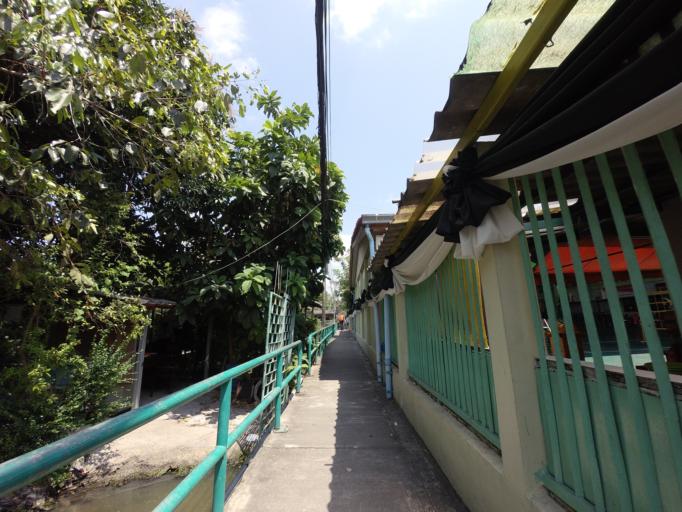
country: TH
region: Bangkok
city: Chom Thong
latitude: 13.6546
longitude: 100.4714
